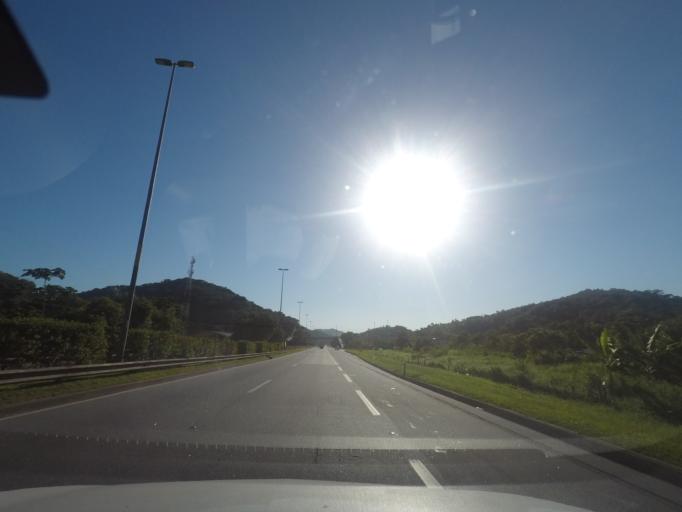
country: BR
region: Rio de Janeiro
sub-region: Petropolis
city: Petropolis
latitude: -22.6537
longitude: -43.1545
